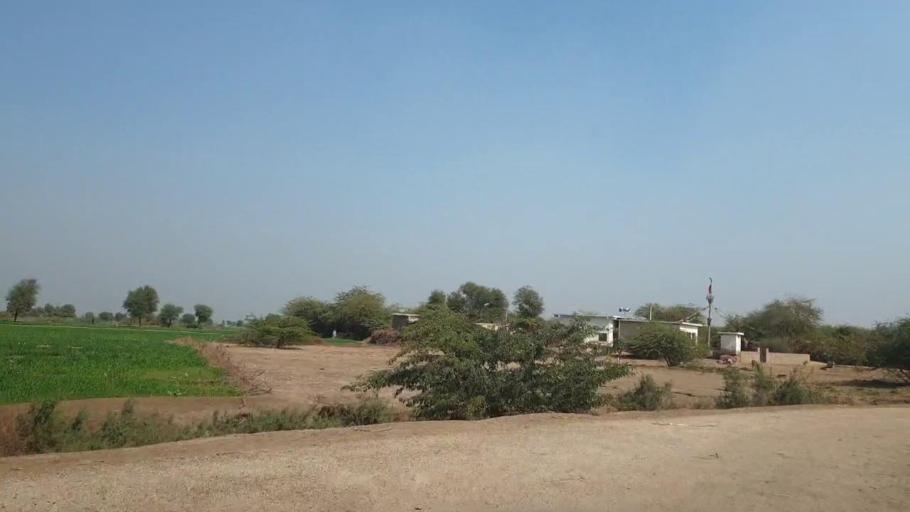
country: PK
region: Sindh
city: Tando Allahyar
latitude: 25.5545
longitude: 68.7185
